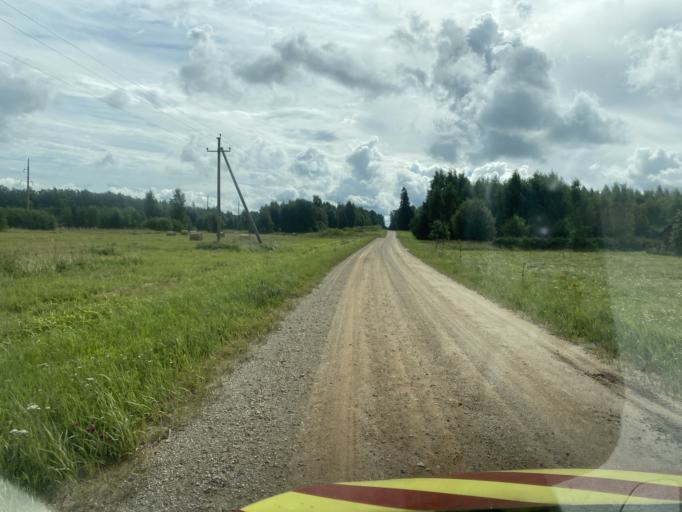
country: EE
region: Viljandimaa
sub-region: Karksi vald
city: Karksi-Nuia
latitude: 58.0872
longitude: 25.4940
